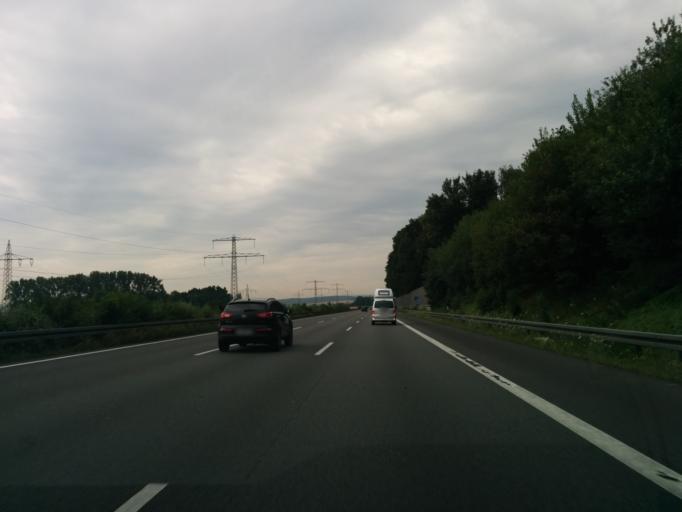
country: DE
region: Lower Saxony
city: Rosdorf
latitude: 51.5016
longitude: 9.8774
